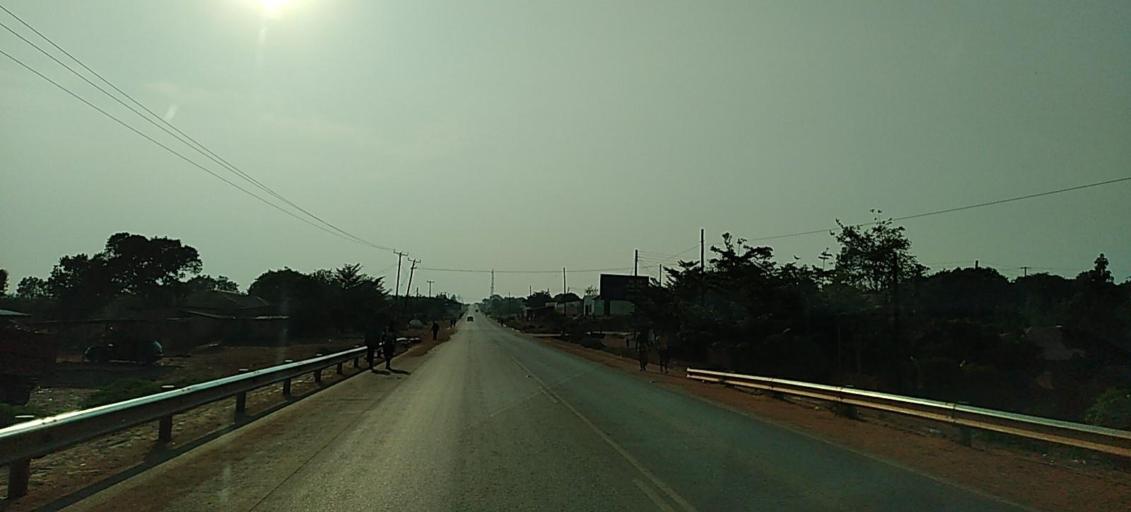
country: ZM
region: North-Western
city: Solwezi
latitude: -12.1889
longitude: 26.4324
